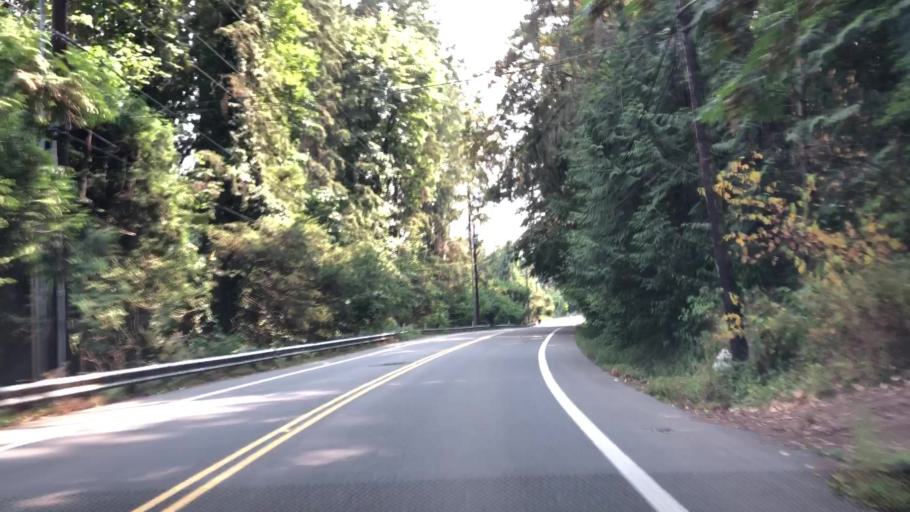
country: US
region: Washington
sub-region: King County
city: Kenmore
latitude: 47.7720
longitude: -122.2487
